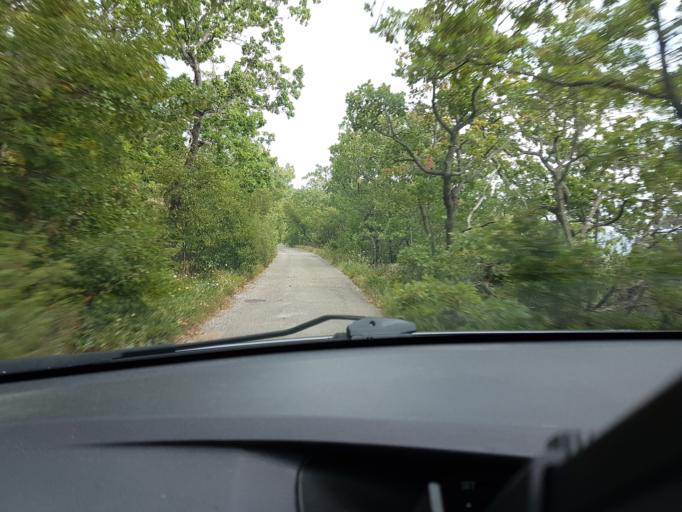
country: HR
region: Primorsko-Goranska
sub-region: Grad Crikvenica
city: Crikvenica
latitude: 45.2298
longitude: 14.7049
